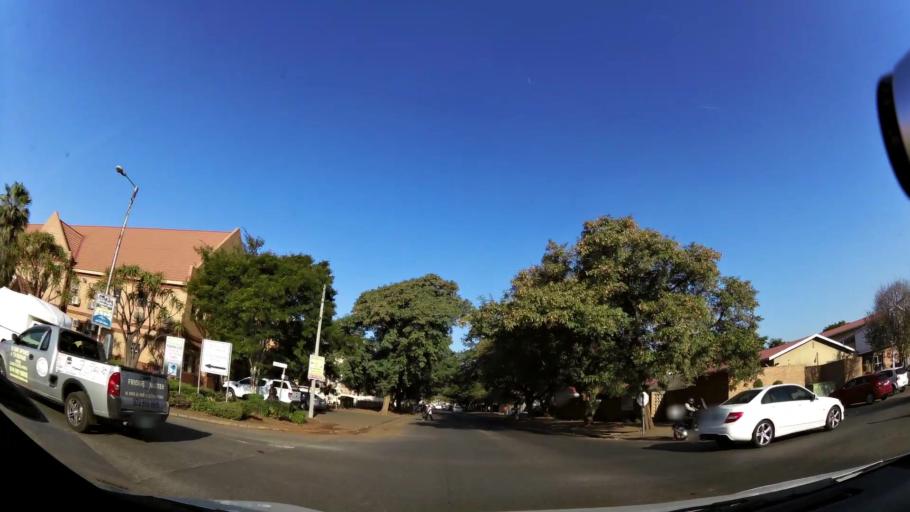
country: ZA
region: North-West
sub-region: Bojanala Platinum District Municipality
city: Rustenburg
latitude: -25.6720
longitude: 27.2388
